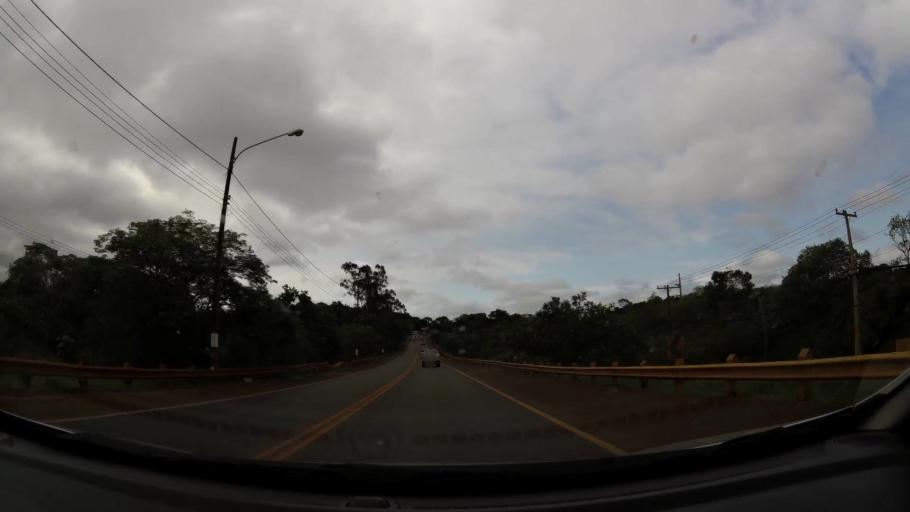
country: PY
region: Alto Parana
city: Ciudad del Este
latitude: -25.4172
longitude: -54.6358
